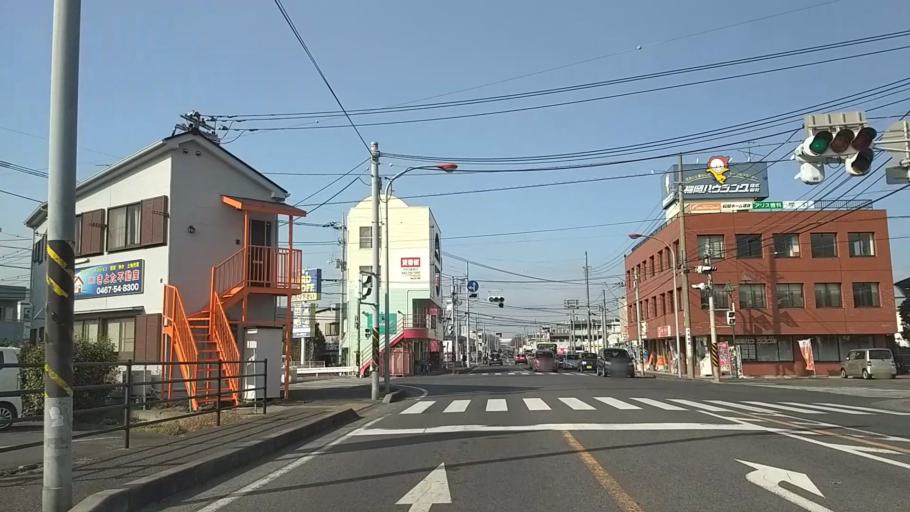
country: JP
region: Kanagawa
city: Chigasaki
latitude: 35.3425
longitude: 139.4123
